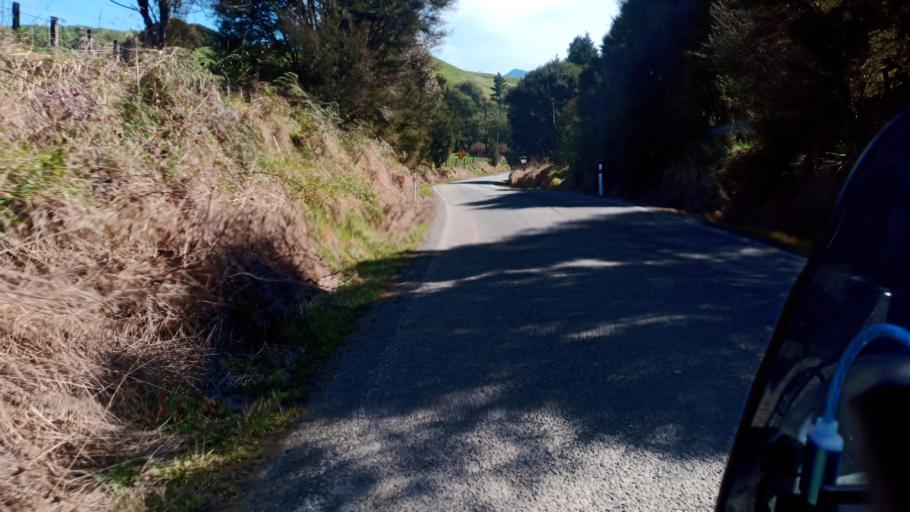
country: NZ
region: Gisborne
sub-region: Gisborne District
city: Gisborne
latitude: -37.9997
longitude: 178.3148
